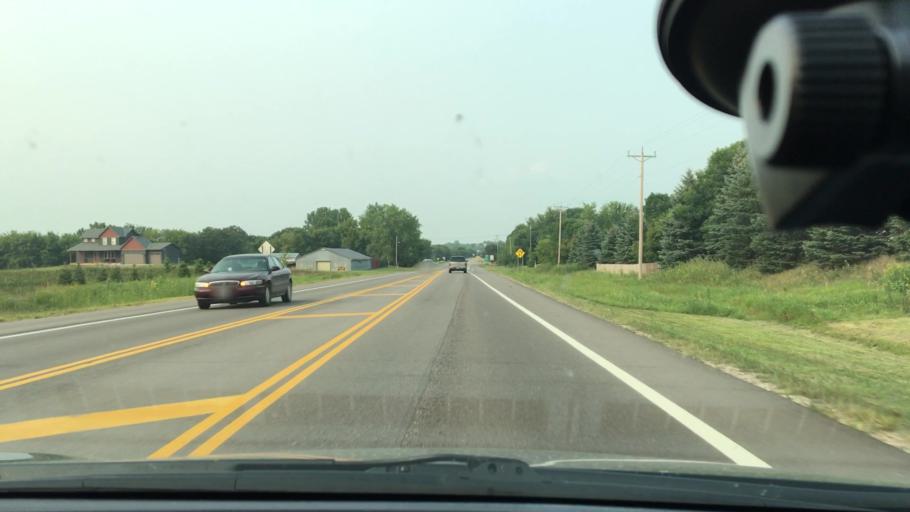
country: US
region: Minnesota
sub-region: Wright County
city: Saint Michael
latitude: 45.2038
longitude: -93.6801
